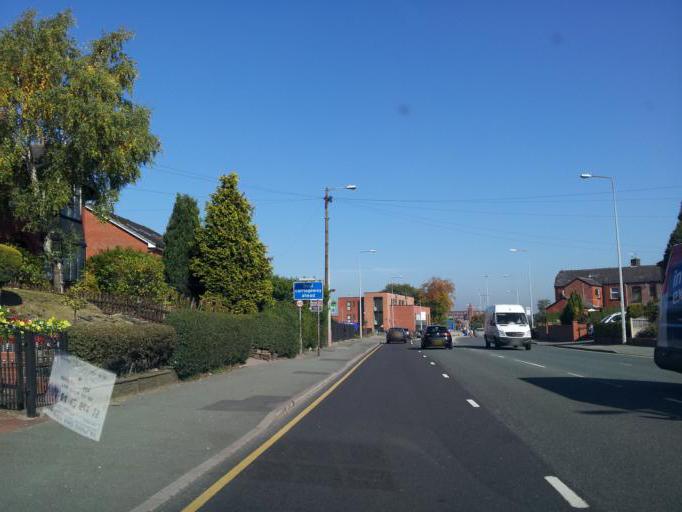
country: GB
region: England
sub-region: Manchester
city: Failsworth
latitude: 53.5243
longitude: -2.1637
